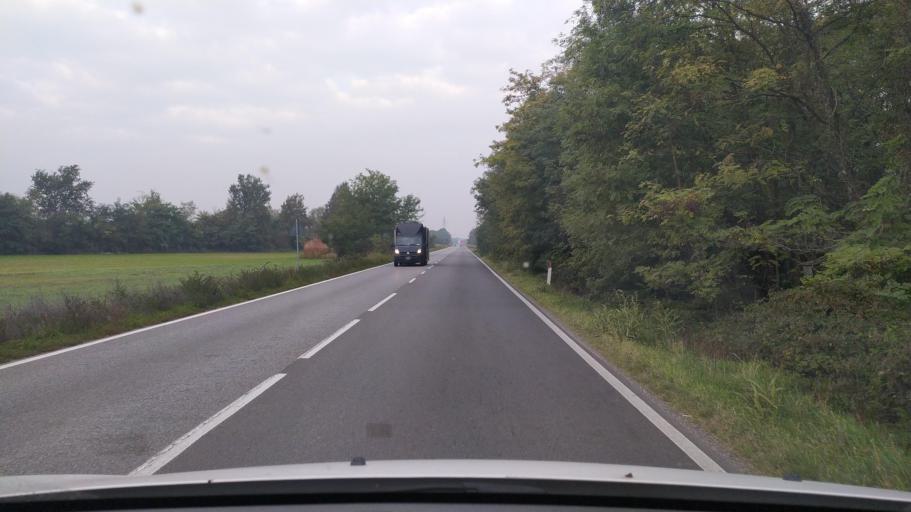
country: IT
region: Lombardy
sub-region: Citta metropolitana di Milano
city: Sedriano
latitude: 45.4673
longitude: 8.9661
